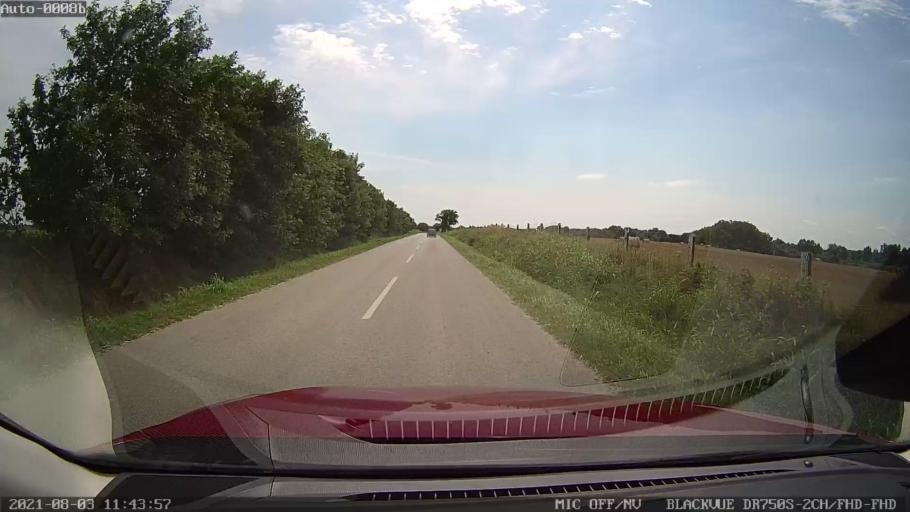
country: HR
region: Osjecko-Baranjska
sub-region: Grad Osijek
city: Bilje
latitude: 45.6058
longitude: 18.7662
